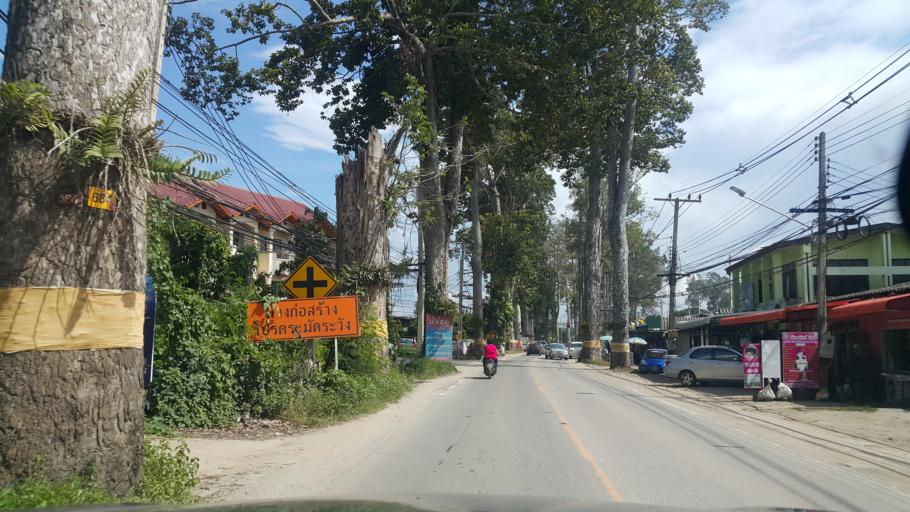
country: TH
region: Chiang Mai
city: Saraphi
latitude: 18.7309
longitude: 99.0219
